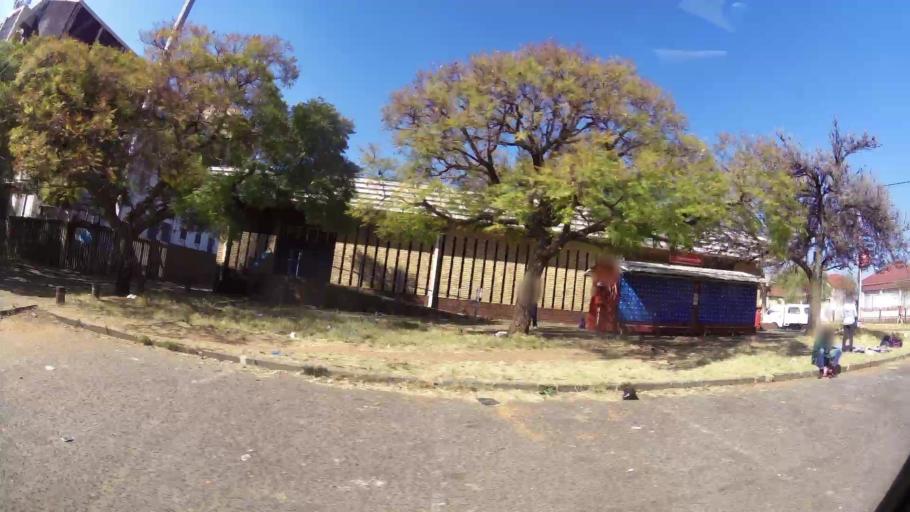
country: ZA
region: Gauteng
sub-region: City of Johannesburg Metropolitan Municipality
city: Johannesburg
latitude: -26.2469
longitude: 28.0396
